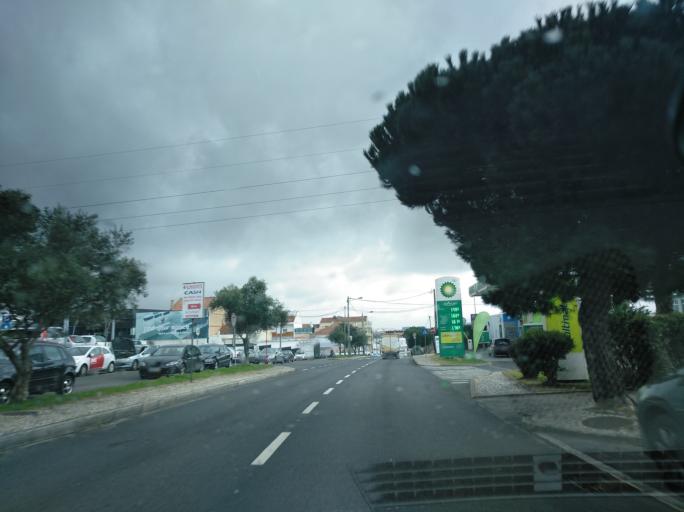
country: PT
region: Lisbon
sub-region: Odivelas
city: Famoes
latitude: 38.7860
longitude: -9.2084
